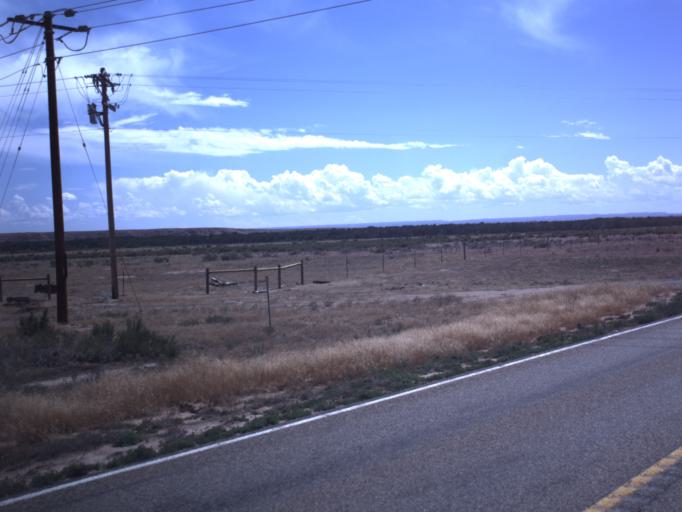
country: US
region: Utah
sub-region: Uintah County
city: Naples
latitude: 40.1245
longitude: -109.6641
